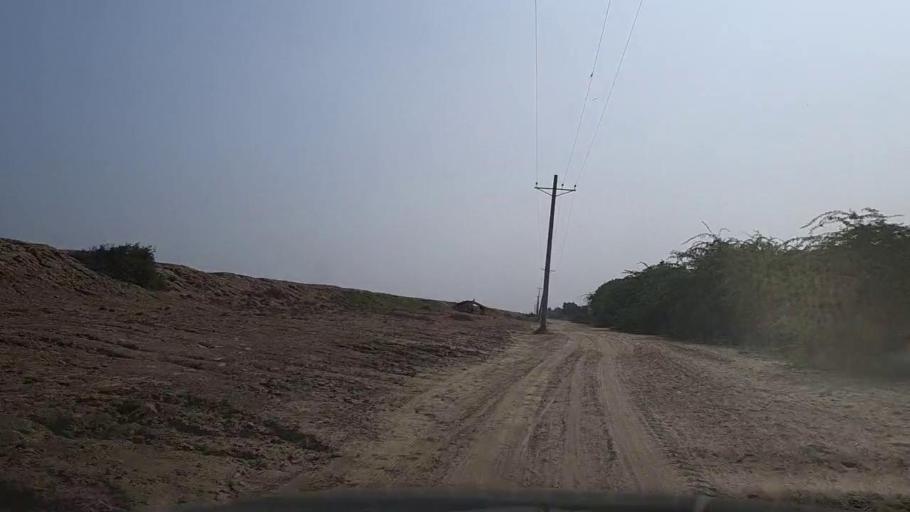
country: PK
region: Sindh
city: Thatta
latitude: 24.5608
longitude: 67.9141
